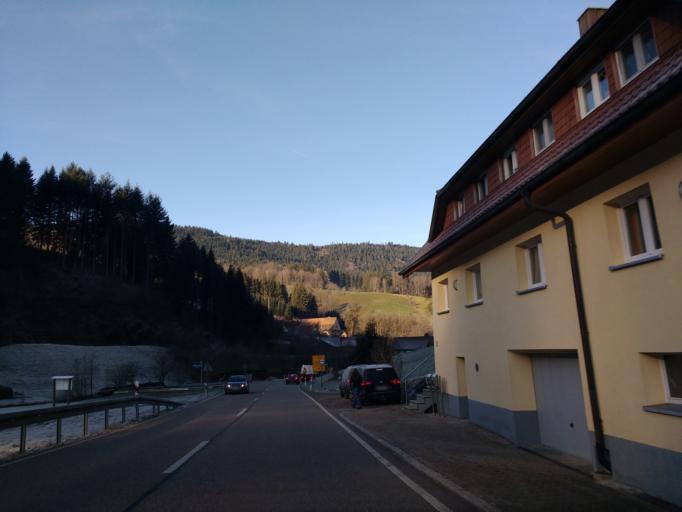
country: DE
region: Baden-Wuerttemberg
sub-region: Freiburg Region
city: Bad Peterstal-Griesbach
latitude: 48.4298
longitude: 8.1789
